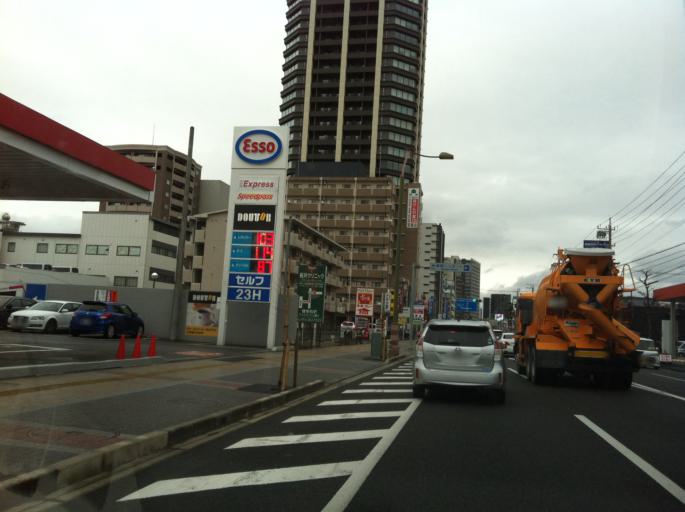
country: JP
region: Shizuoka
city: Shizuoka-shi
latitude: 34.9806
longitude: 138.4123
